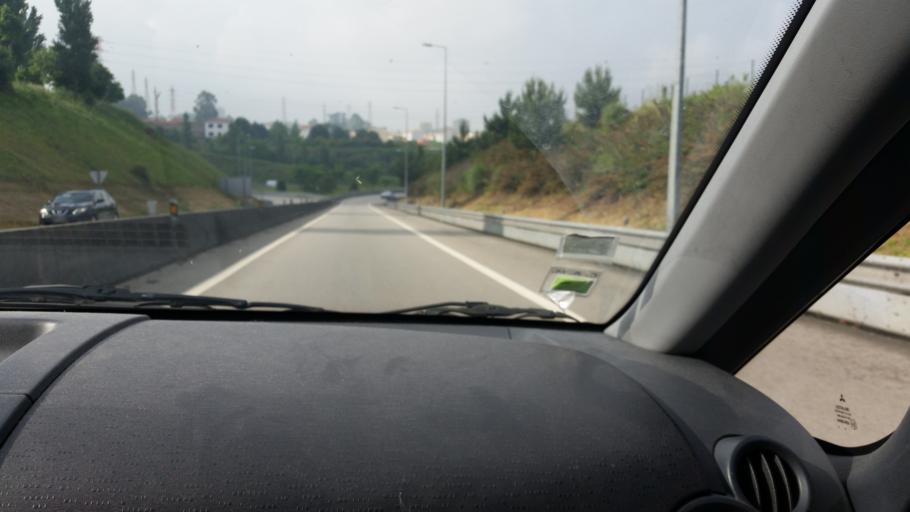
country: PT
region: Porto
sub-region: Matosinhos
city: Guifoes
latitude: 41.2038
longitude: -8.6546
